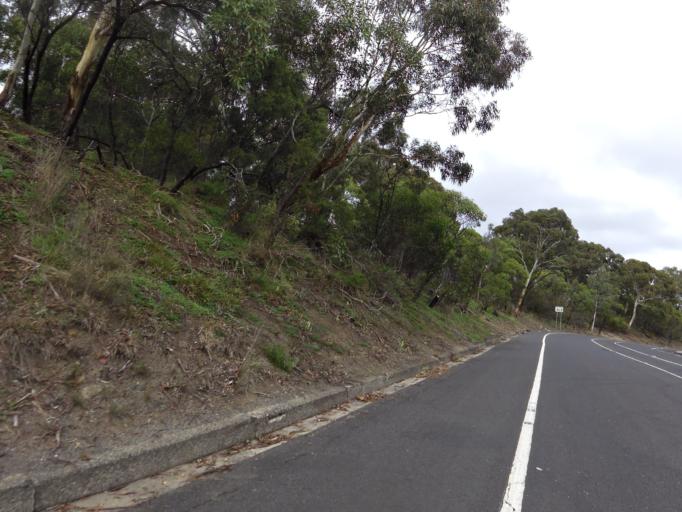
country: AU
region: Victoria
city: Abbotsford
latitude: -37.8037
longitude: 145.0088
